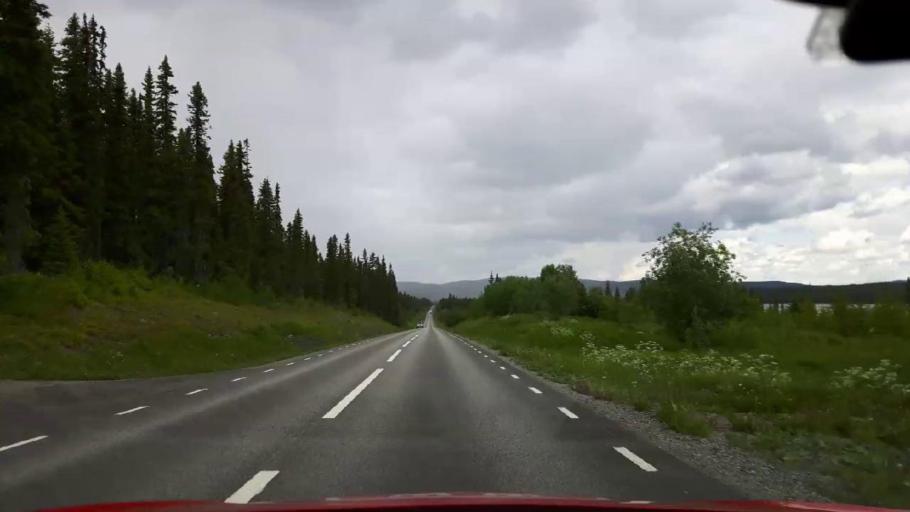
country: SE
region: Jaemtland
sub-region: Krokoms Kommun
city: Krokom
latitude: 63.7056
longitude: 14.3128
